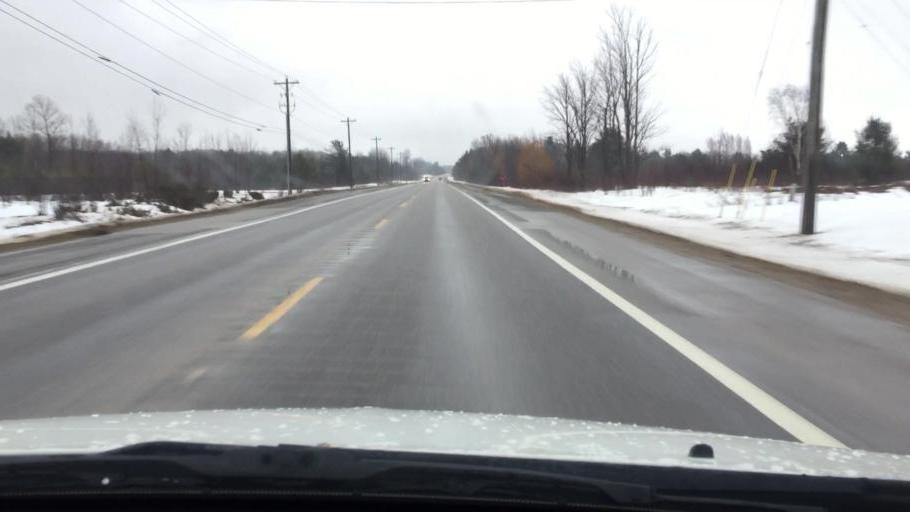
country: US
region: Michigan
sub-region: Charlevoix County
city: Charlevoix
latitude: 45.2781
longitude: -85.2279
